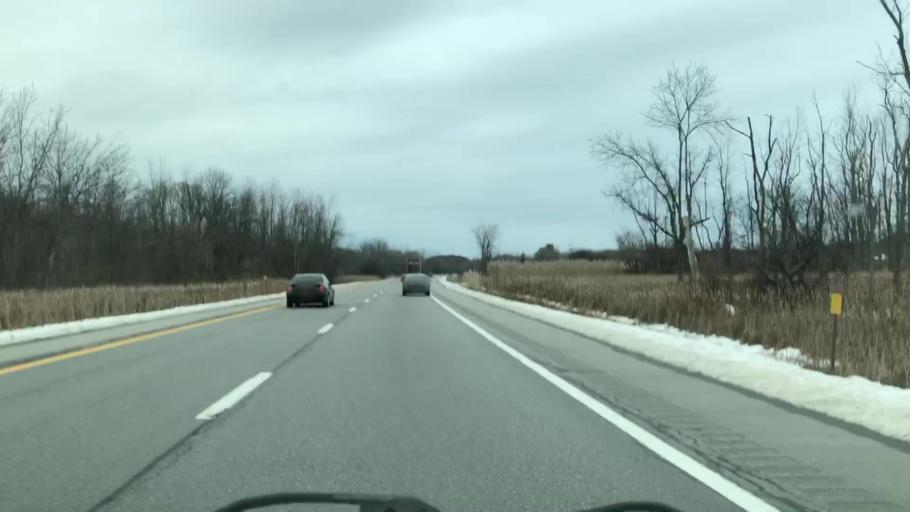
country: US
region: New York
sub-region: Monroe County
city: Spencerport
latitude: 43.1169
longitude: -77.7658
